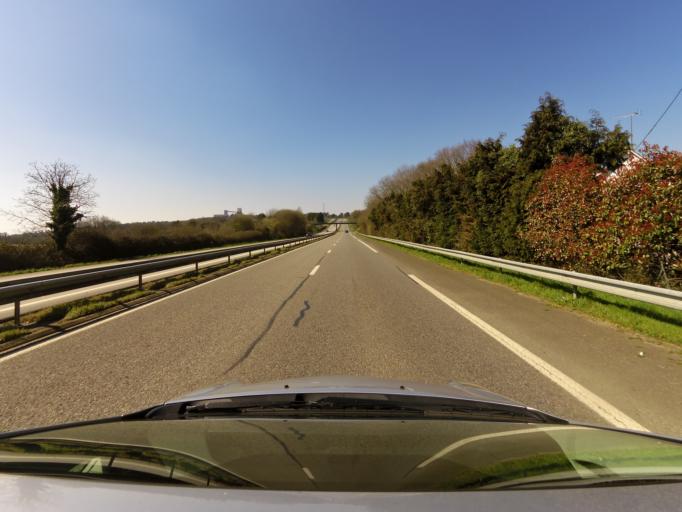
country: FR
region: Brittany
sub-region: Departement du Morbihan
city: Bignan
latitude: 47.9180
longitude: -2.7311
